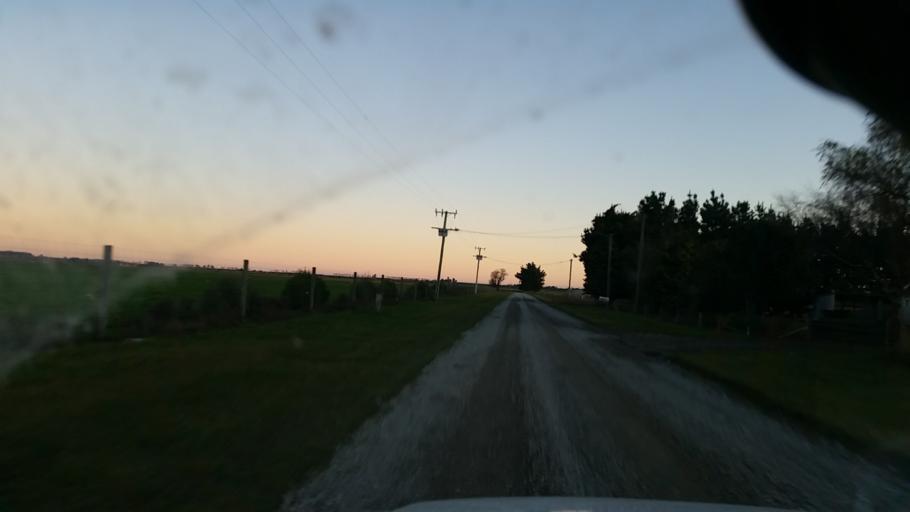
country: NZ
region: Canterbury
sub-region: Ashburton District
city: Tinwald
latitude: -44.0583
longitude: 171.6615
